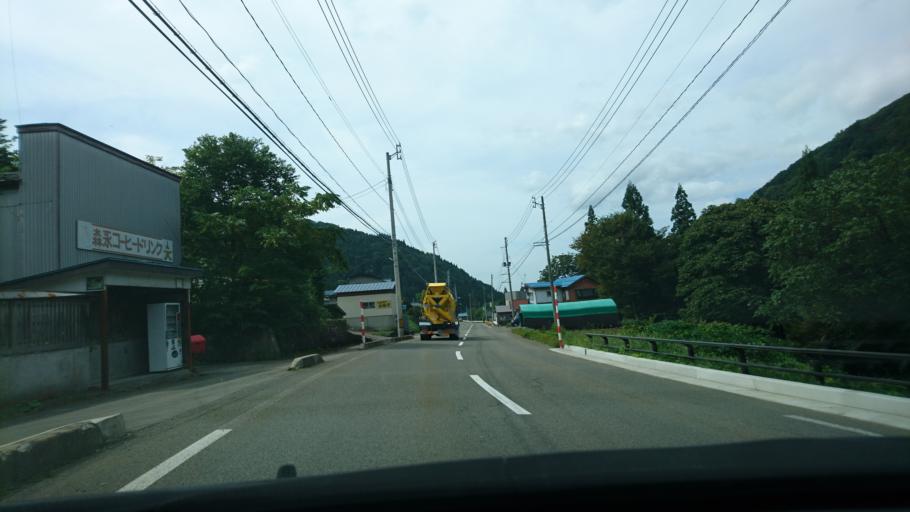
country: JP
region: Akita
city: Yuzawa
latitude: 39.1724
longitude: 140.6774
